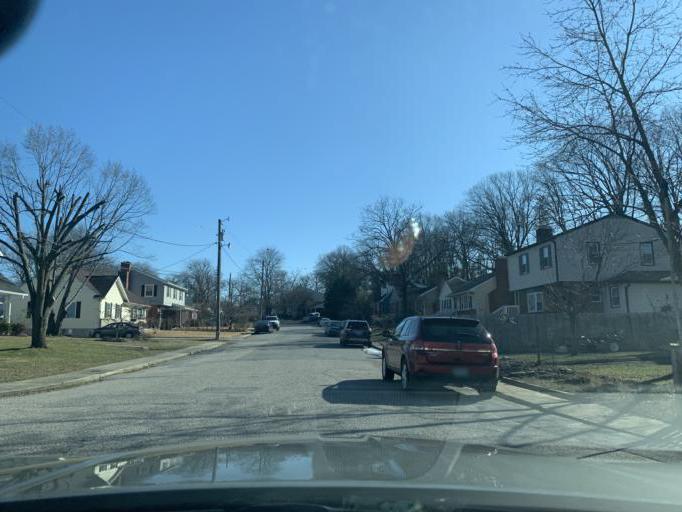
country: US
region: Maryland
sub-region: Anne Arundel County
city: Glen Burnie
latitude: 39.1668
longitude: -76.6341
